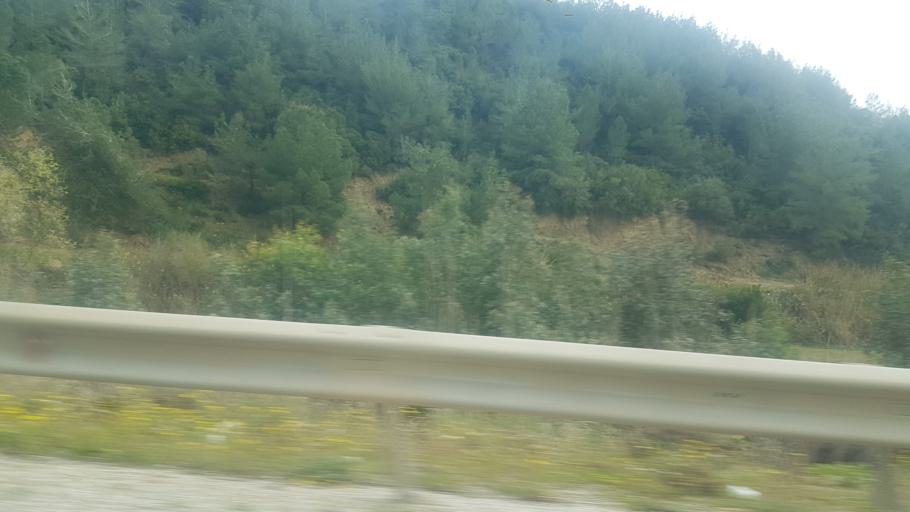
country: TR
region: Mersin
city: Yenice
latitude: 37.0916
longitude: 35.1442
